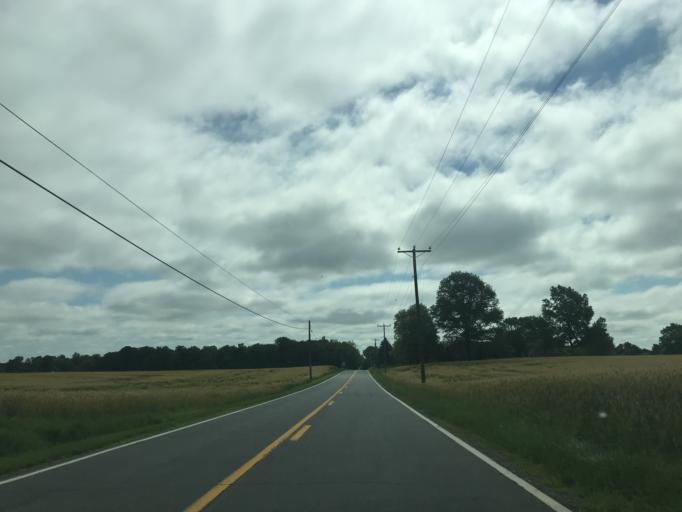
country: US
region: Maryland
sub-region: Caroline County
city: Ridgely
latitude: 38.8851
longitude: -75.9752
